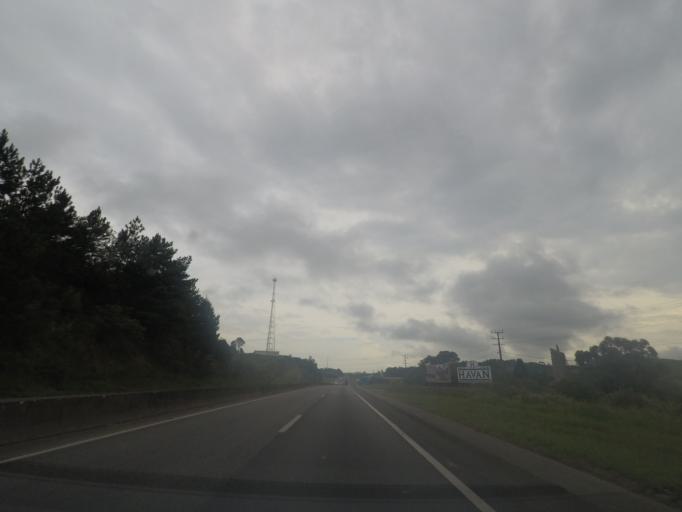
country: BR
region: Parana
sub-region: Campina Grande Do Sul
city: Campina Grande do Sul
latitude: -25.3243
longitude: -49.0257
